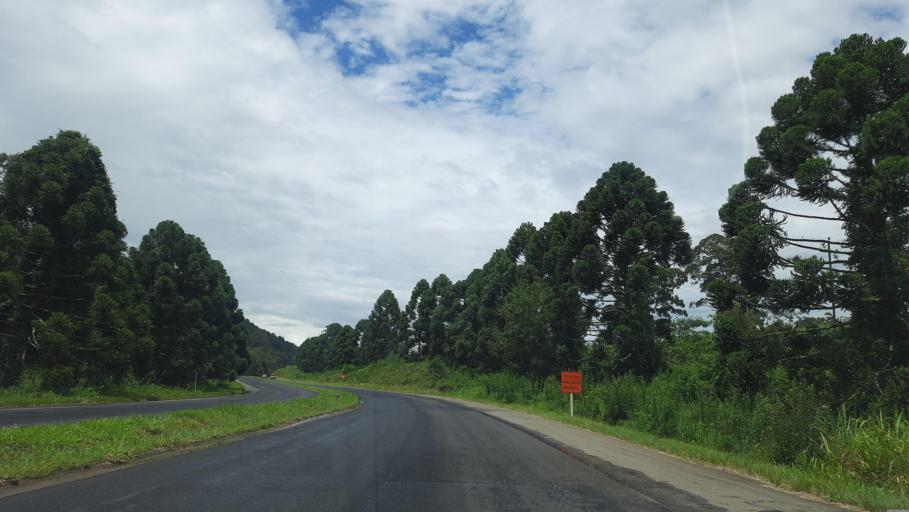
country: BR
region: Minas Gerais
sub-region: Pocos De Caldas
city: Pocos de Caldas
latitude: -21.8092
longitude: -46.6550
